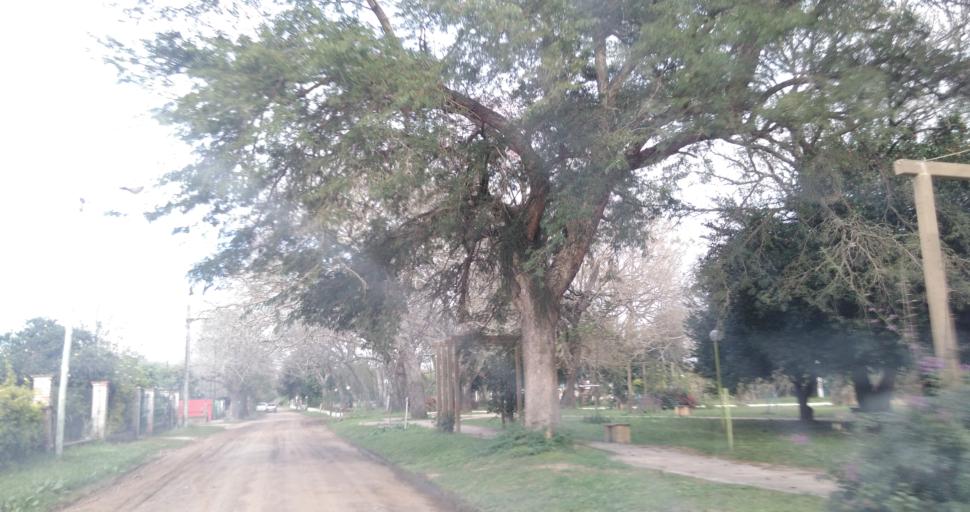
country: AR
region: Chaco
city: Colonia Benitez
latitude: -27.3298
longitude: -58.9553
